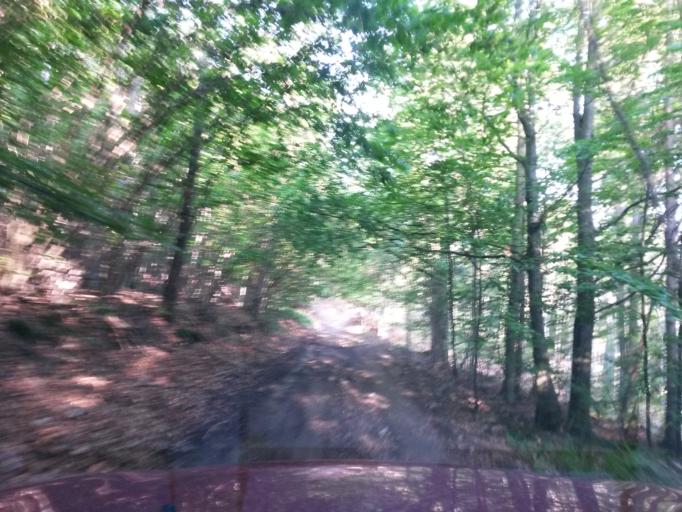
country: SK
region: Kosicky
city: Moldava nad Bodvou
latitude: 48.7401
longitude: 21.0358
